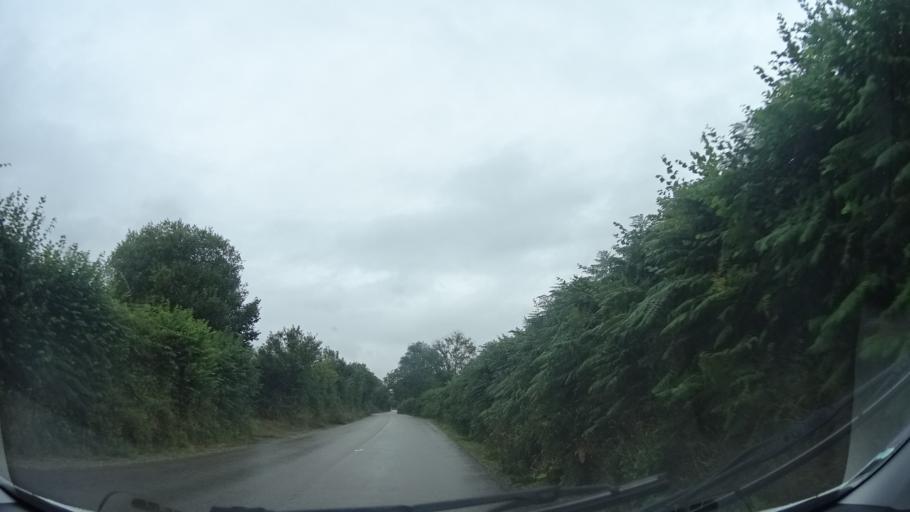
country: FR
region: Lower Normandy
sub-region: Departement de la Manche
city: Urville-Nacqueville
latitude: 49.6028
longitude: -1.7398
